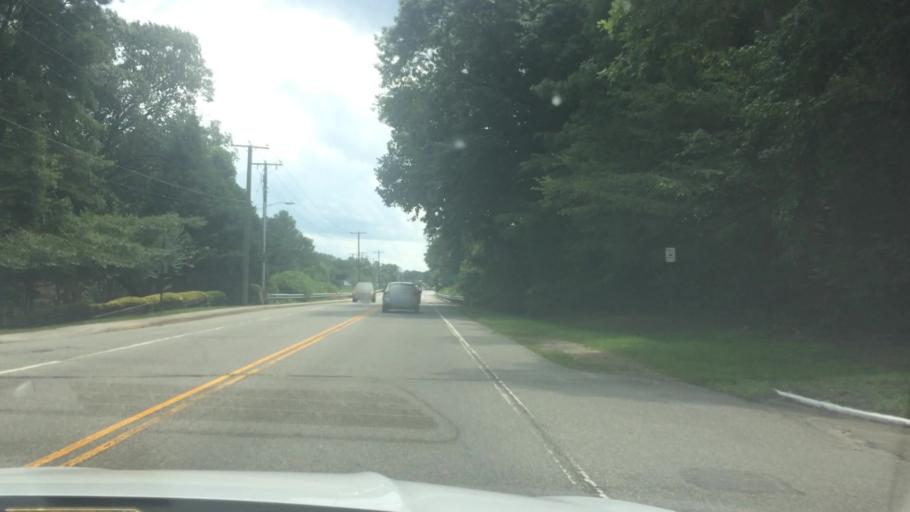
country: US
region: Virginia
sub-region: City of Williamsburg
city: Williamsburg
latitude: 37.2763
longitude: -76.6811
